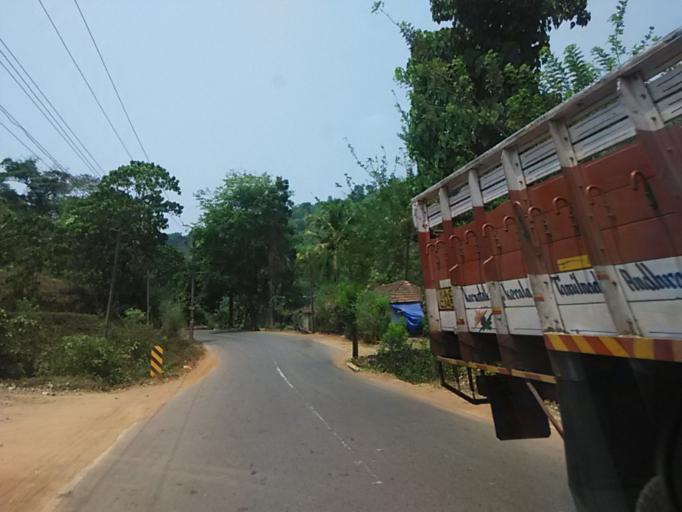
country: IN
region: Karnataka
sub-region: Kodagu
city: Virarajendrapet
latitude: 12.0638
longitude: 75.7215
